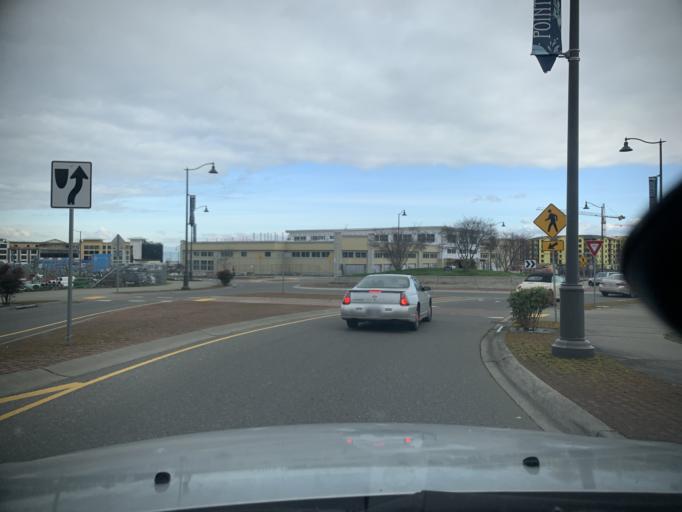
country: US
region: Washington
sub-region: Pierce County
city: Fircrest
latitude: 47.2989
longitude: -122.5091
